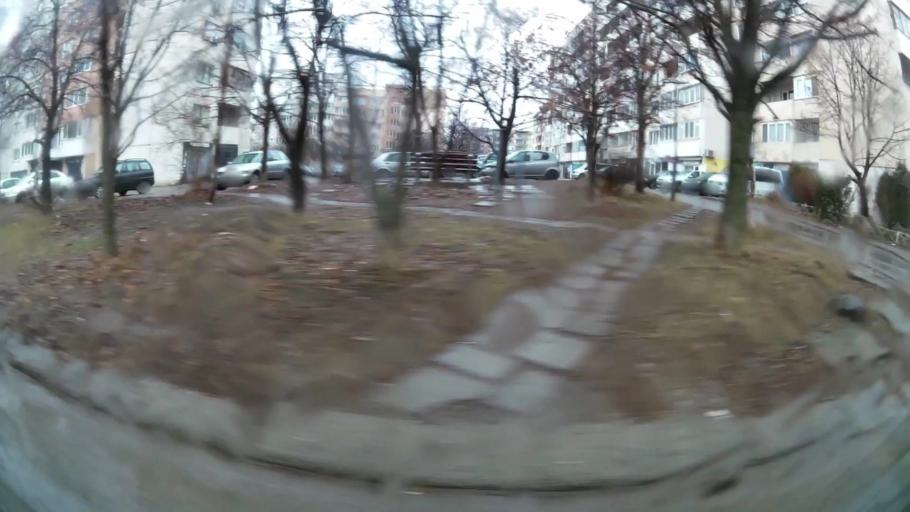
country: BG
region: Sofia-Capital
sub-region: Stolichna Obshtina
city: Sofia
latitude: 42.6513
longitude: 23.3636
